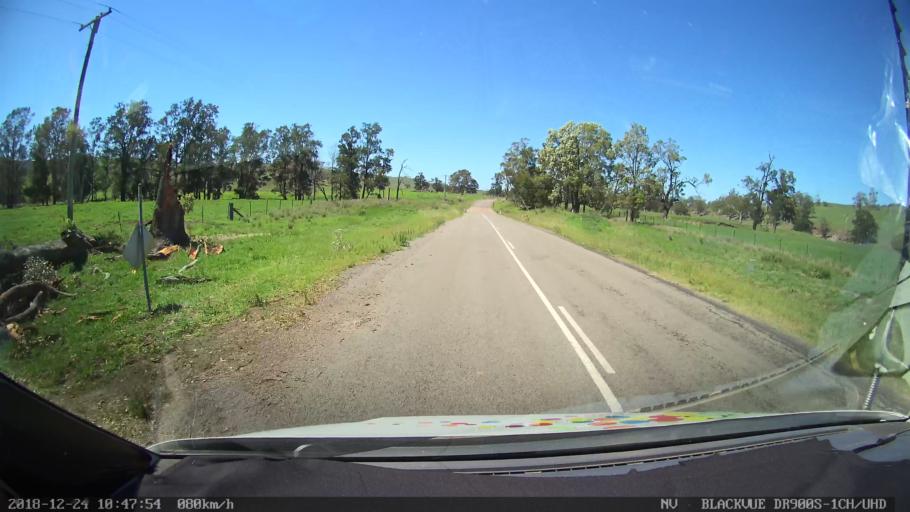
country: AU
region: New South Wales
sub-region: Upper Hunter Shire
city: Merriwa
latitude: -31.9299
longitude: 150.4298
